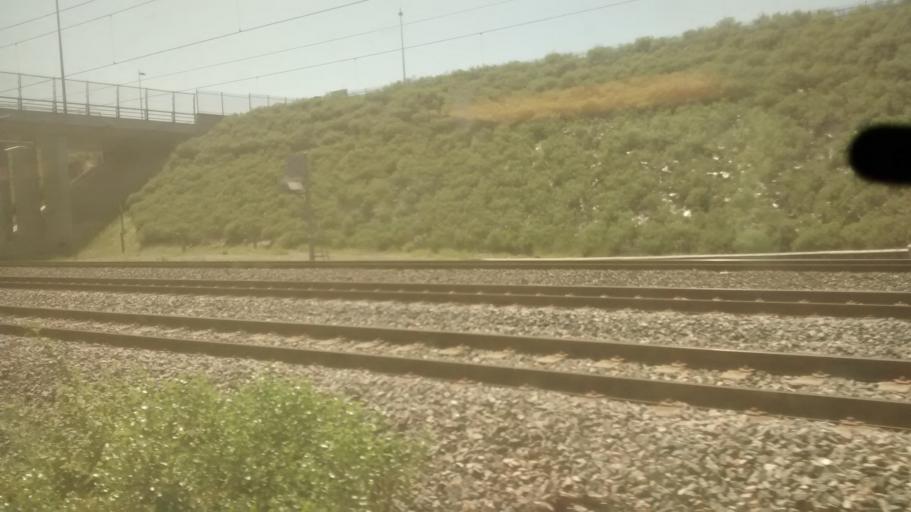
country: FR
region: Rhone-Alpes
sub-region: Departement de la Drome
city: Saint-Marcel-les-Valence
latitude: 44.9892
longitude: 4.9791
